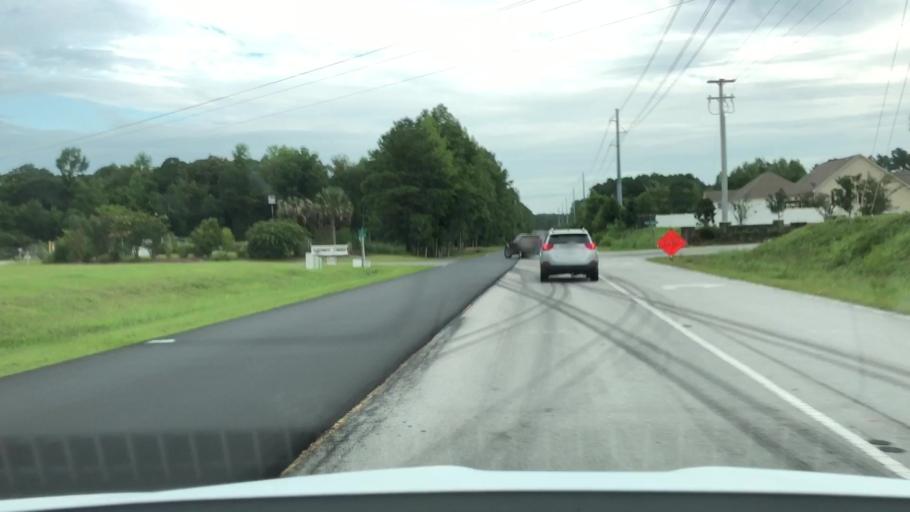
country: US
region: North Carolina
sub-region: Carteret County
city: Cape Carteret
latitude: 34.7612
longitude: -77.0950
